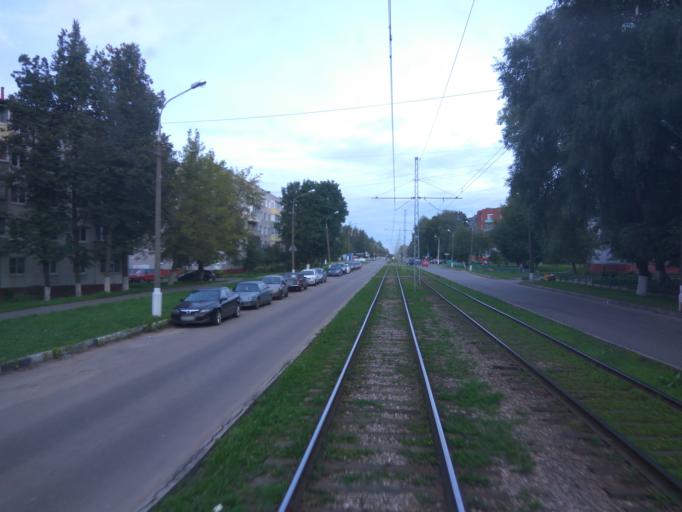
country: RU
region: Moskovskaya
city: Kolomna
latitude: 55.0797
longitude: 38.7664
